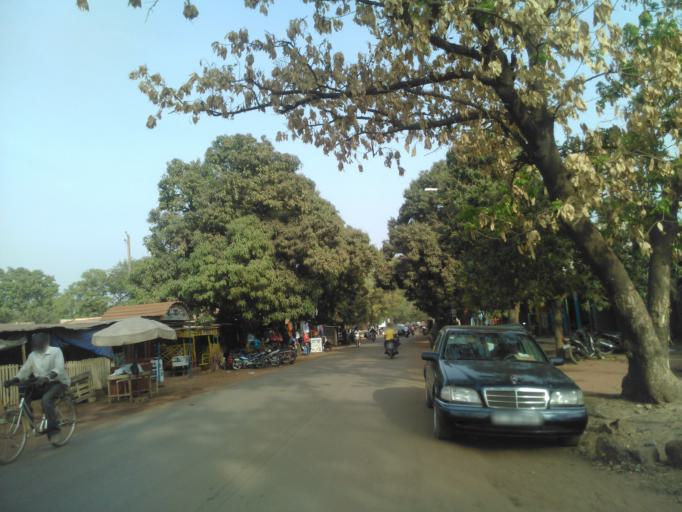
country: BF
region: High-Basins
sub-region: Province du Houet
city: Bobo-Dioulasso
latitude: 11.1736
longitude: -4.3039
